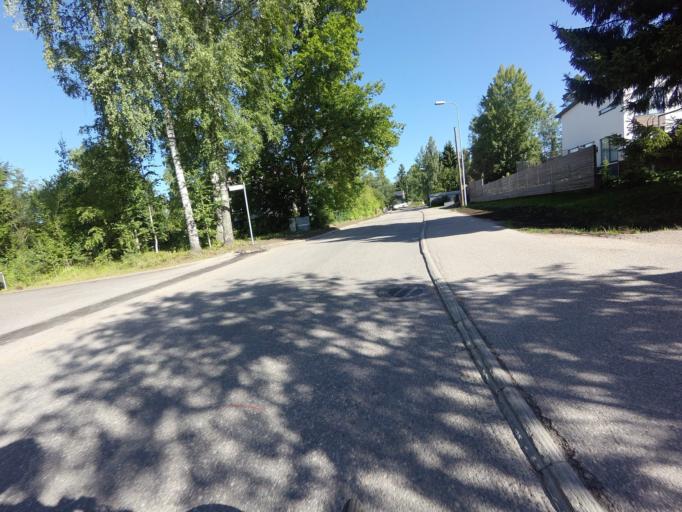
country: FI
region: Uusimaa
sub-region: Helsinki
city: Espoo
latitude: 60.1649
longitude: 24.6716
